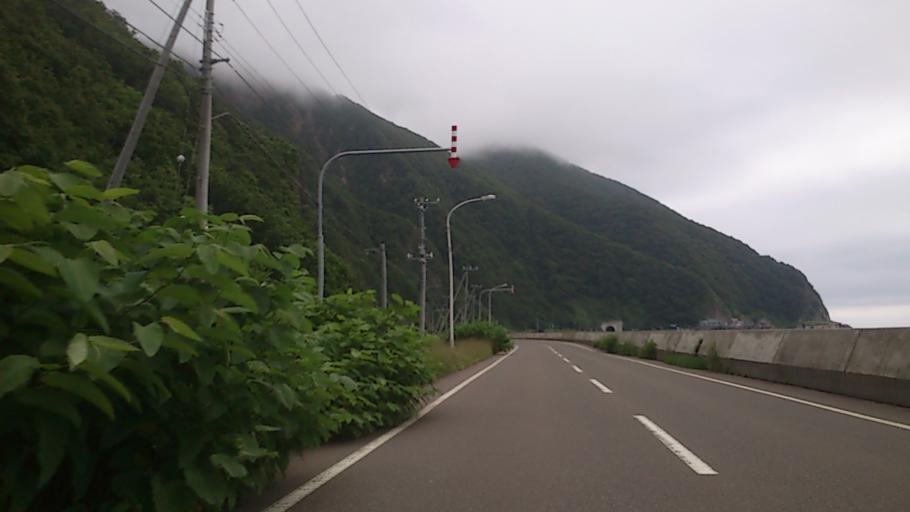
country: JP
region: Hokkaido
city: Kamiiso
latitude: 42.2744
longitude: 139.7857
